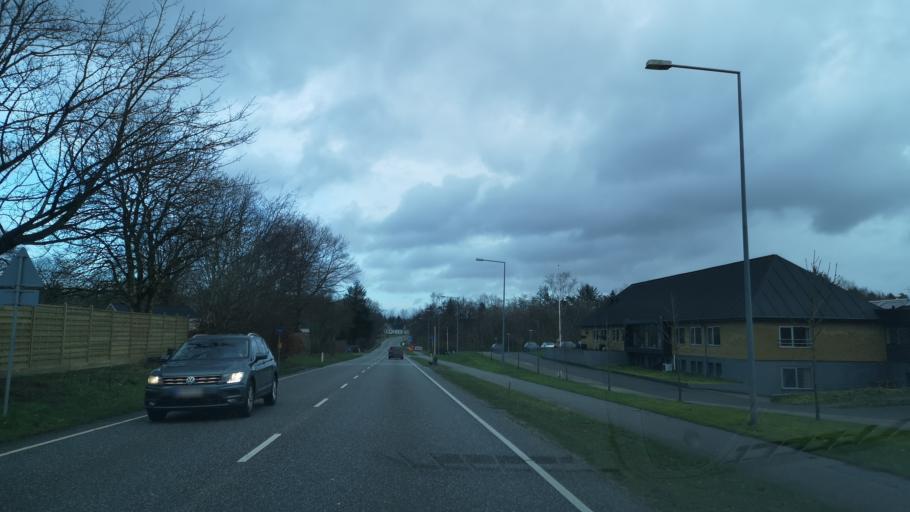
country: DK
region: Central Jutland
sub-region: Herning Kommune
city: Lind
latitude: 56.0129
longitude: 8.9869
